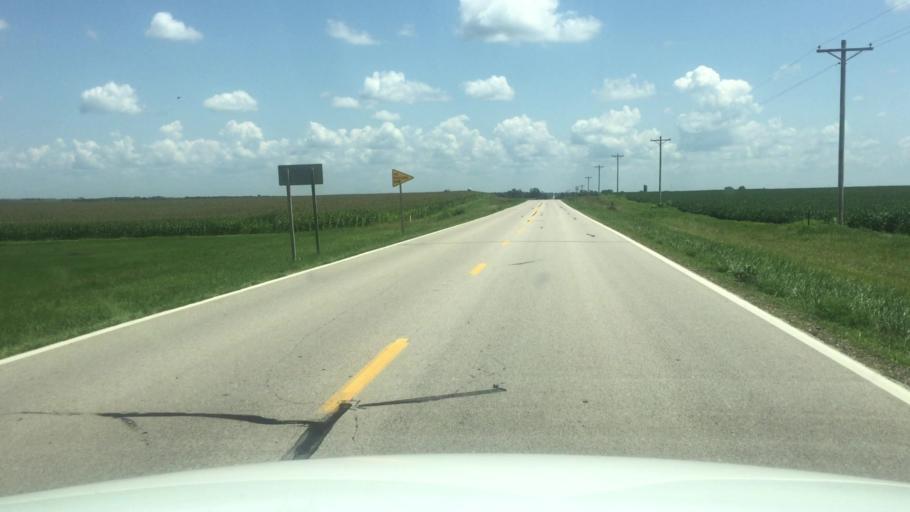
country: US
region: Kansas
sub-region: Brown County
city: Horton
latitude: 39.6674
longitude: -95.6005
